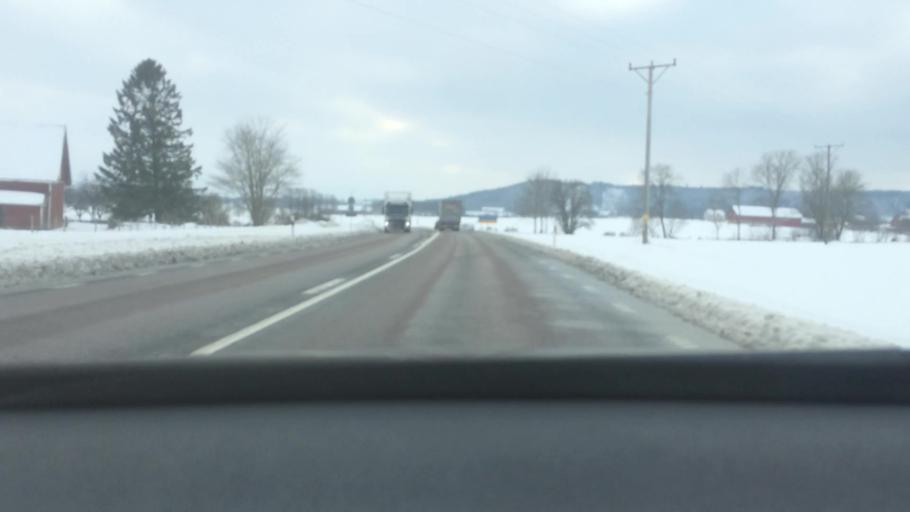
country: SE
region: Vaestra Goetaland
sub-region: Falkopings Kommun
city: Falkoeping
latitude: 58.2104
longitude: 13.5614
